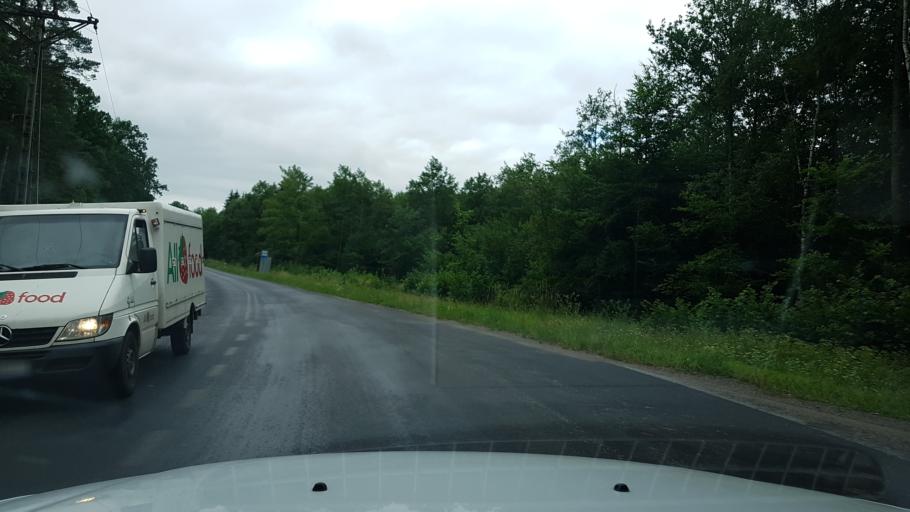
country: PL
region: West Pomeranian Voivodeship
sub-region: Powiat gryficki
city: Gryfice
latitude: 53.9387
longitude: 15.2556
